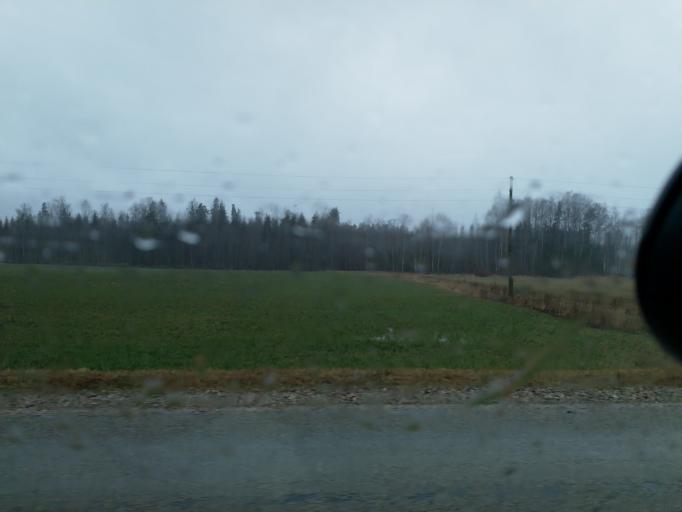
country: LV
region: Saldus Rajons
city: Saldus
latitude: 56.7933
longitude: 22.3175
